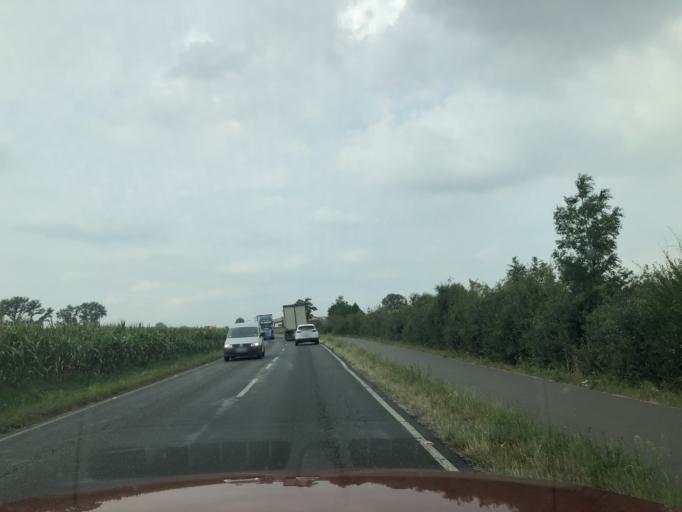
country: PL
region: Greater Poland Voivodeship
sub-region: Powiat leszczynski
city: Swieciechowa
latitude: 51.8814
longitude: 16.4504
